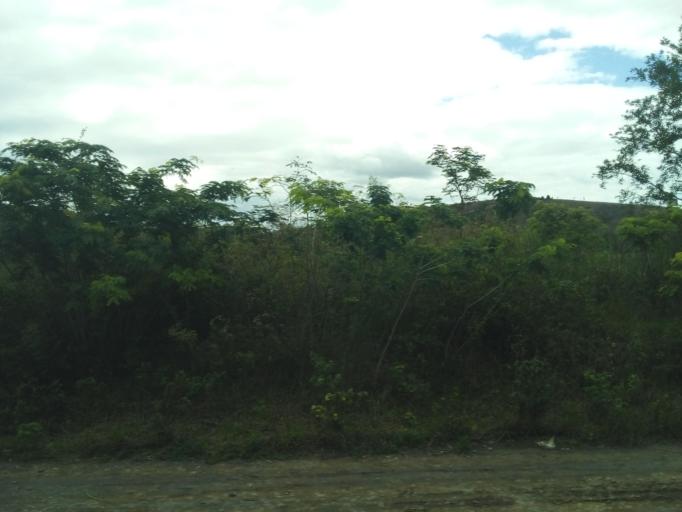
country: BR
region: Minas Gerais
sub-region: Governador Valadares
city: Governador Valadares
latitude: -19.0824
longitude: -42.1607
